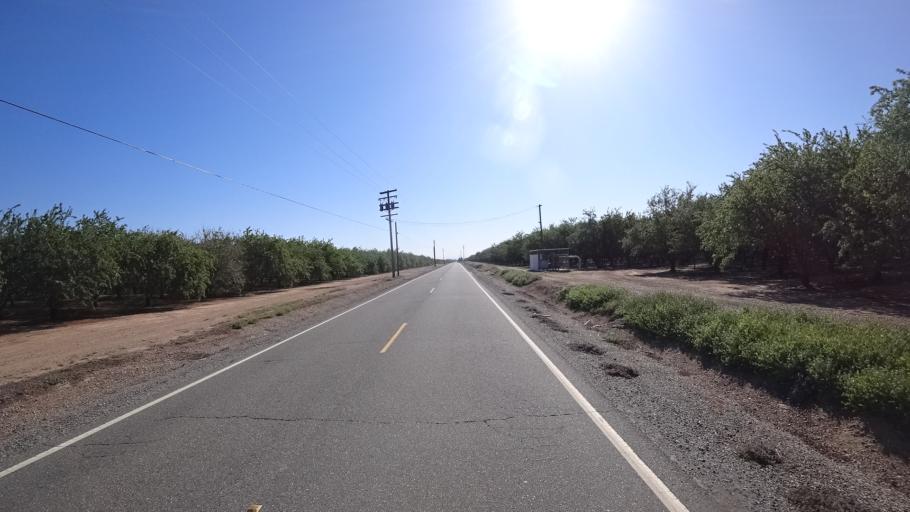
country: US
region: California
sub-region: Glenn County
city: Hamilton City
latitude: 39.7091
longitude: -122.0481
